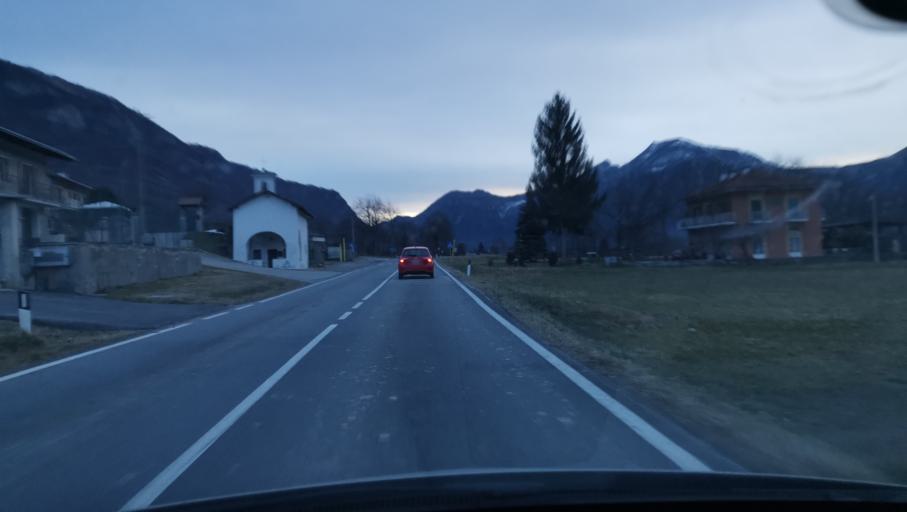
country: IT
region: Piedmont
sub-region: Provincia di Cuneo
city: Demonte
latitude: 44.3169
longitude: 7.3132
